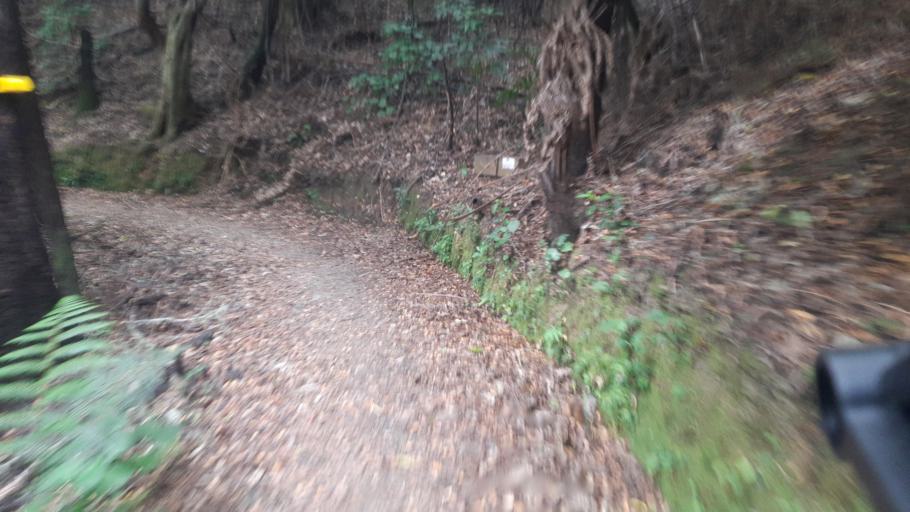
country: NZ
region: Marlborough
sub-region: Marlborough District
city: Picton
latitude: -41.2659
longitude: 173.9992
